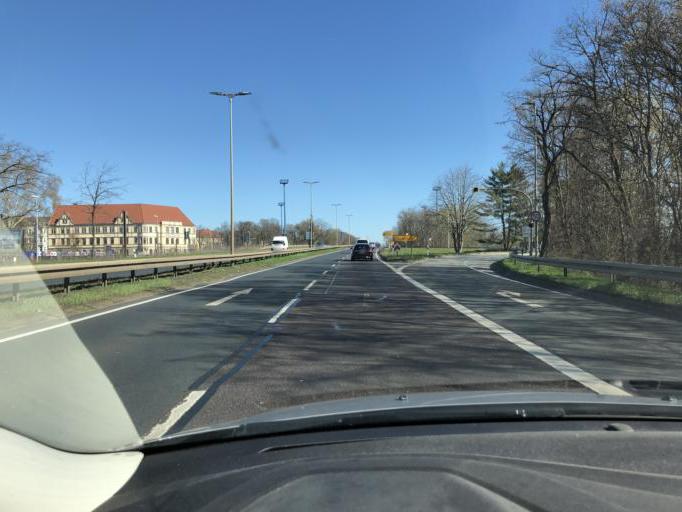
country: DE
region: Saxony-Anhalt
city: Magdeburg
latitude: 52.1303
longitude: 11.6221
